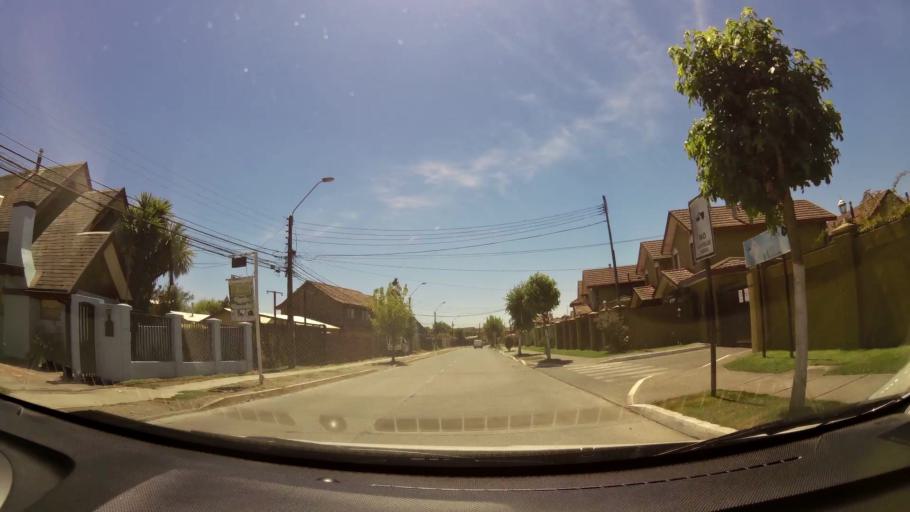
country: CL
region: Biobio
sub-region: Provincia de Concepcion
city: Talcahuano
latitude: -36.7569
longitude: -73.0869
